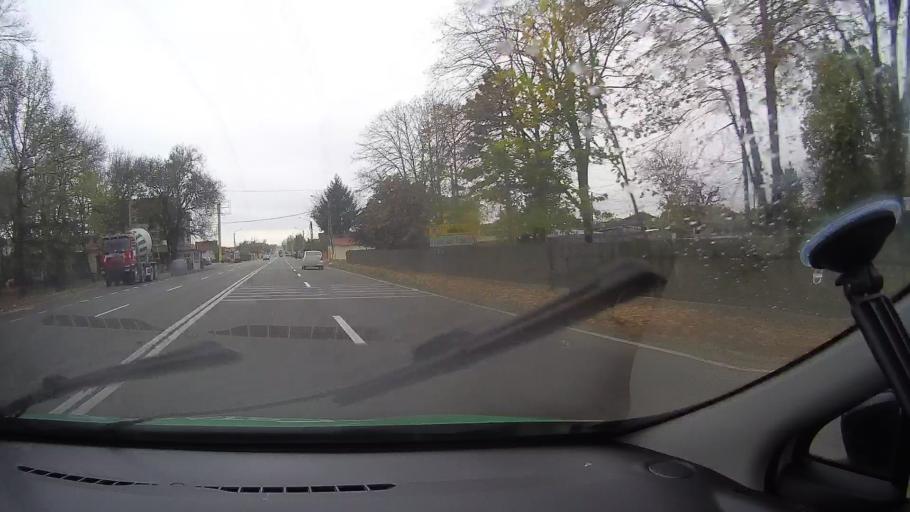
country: RO
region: Constanta
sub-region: Comuna Valu lui Traian
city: Valu lui Traian
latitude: 44.1650
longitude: 28.4914
